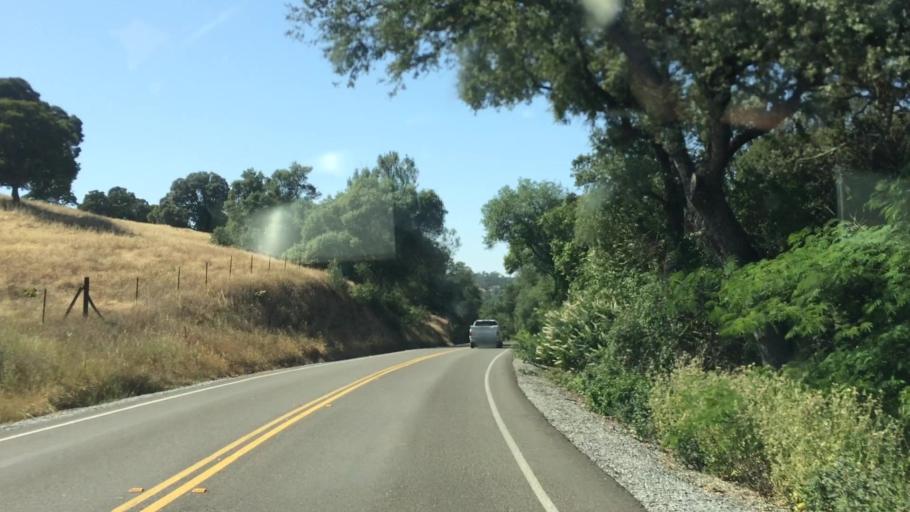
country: US
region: California
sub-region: Amador County
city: Plymouth
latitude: 38.5102
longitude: -120.9481
